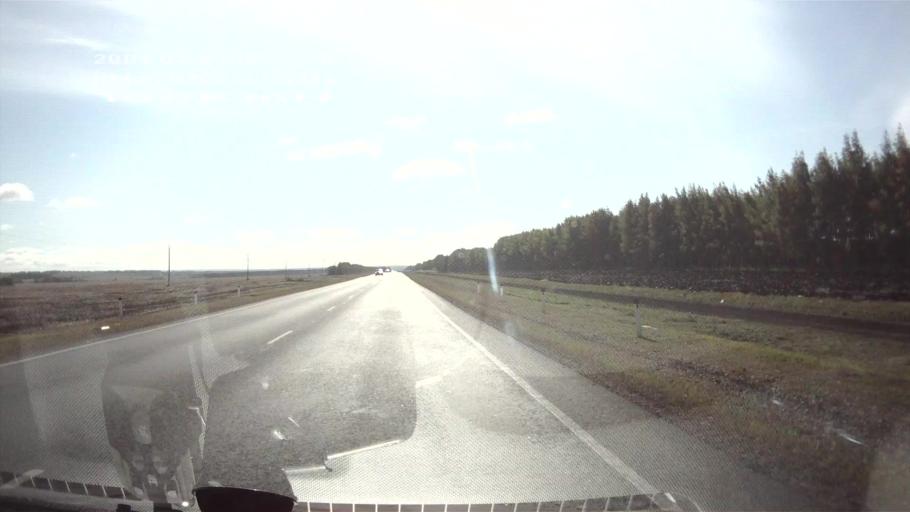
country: RU
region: Ulyanovsk
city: Tsil'na
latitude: 54.5707
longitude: 47.9083
